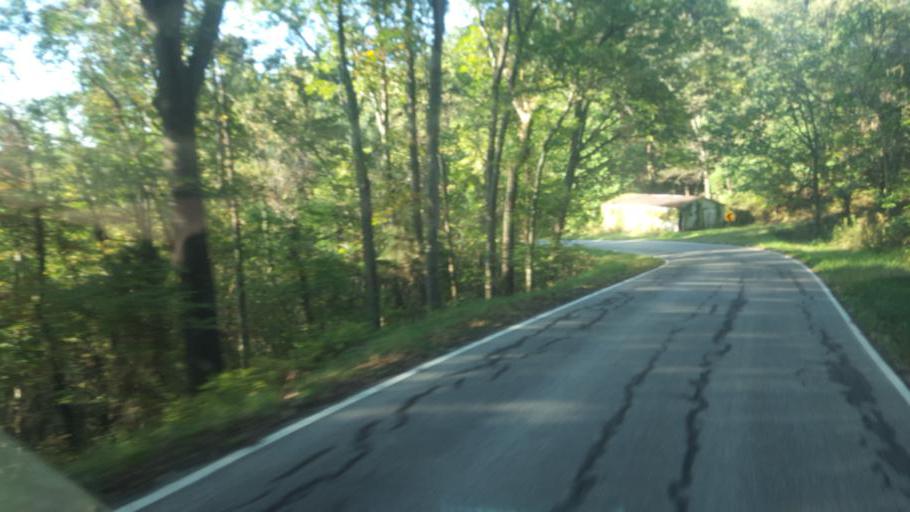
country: US
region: Ohio
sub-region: Adams County
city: Manchester
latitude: 38.5191
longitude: -83.5198
